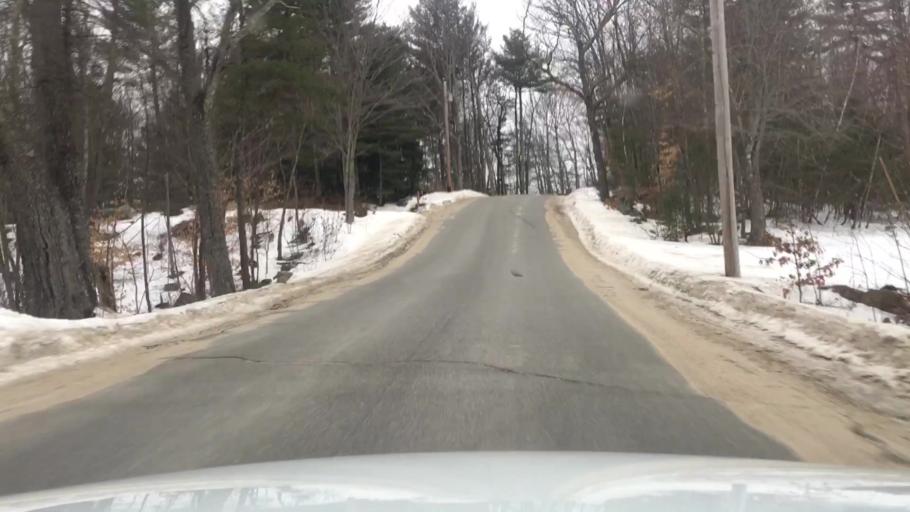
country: US
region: Maine
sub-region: York County
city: Shapleigh
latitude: 43.5040
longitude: -70.8263
